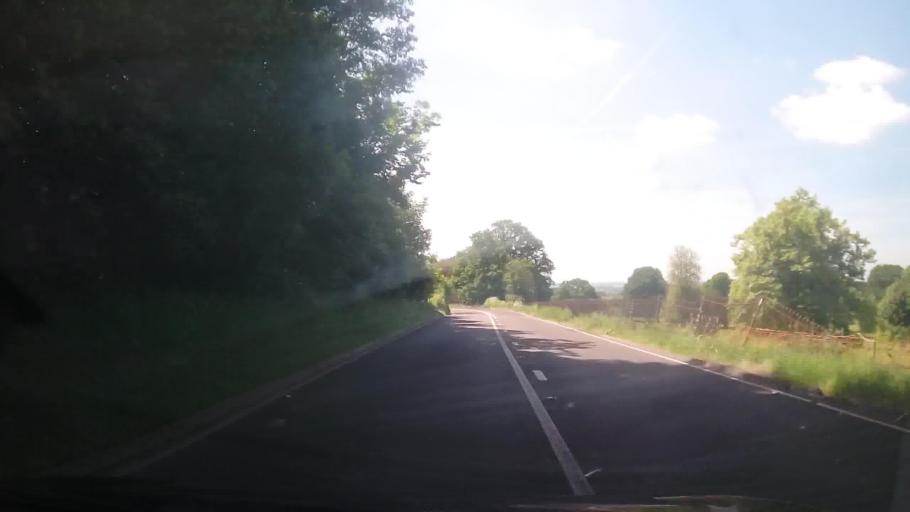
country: GB
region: England
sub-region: Herefordshire
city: Kimbolton
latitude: 52.2673
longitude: -2.7142
